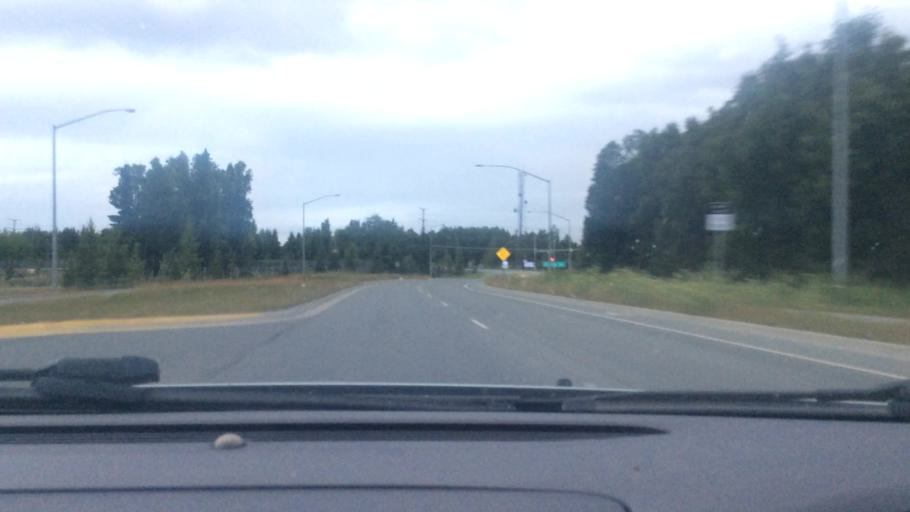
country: US
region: Alaska
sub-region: Anchorage Municipality
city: Anchorage
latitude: 61.1778
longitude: -149.8033
